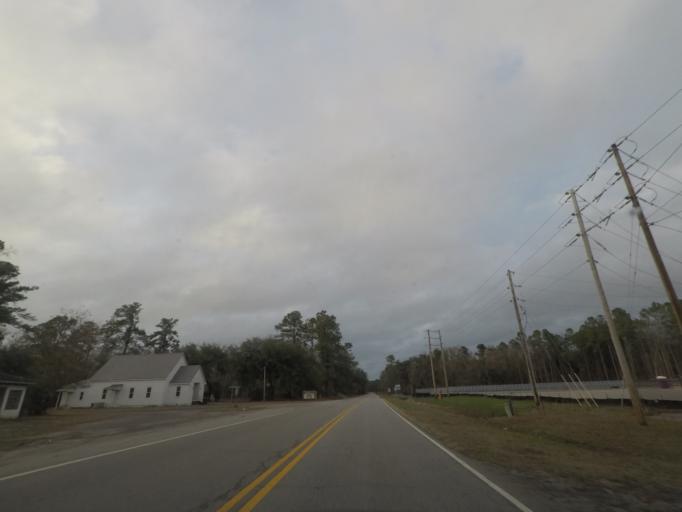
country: US
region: South Carolina
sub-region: Dorchester County
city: Saint George
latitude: 33.0635
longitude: -80.6303
